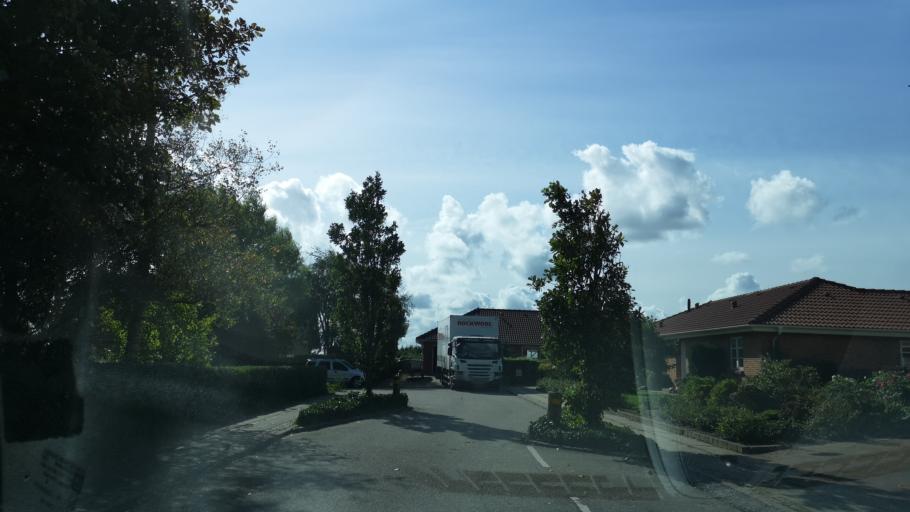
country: DK
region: Central Jutland
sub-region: Ringkobing-Skjern Kommune
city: Skjern
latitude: 55.9834
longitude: 8.5441
